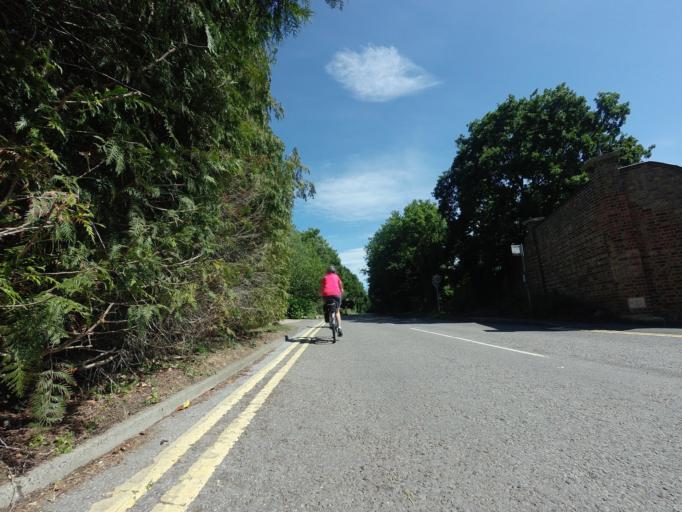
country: GB
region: England
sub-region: Medway
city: Rochester
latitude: 51.4071
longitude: 0.5248
